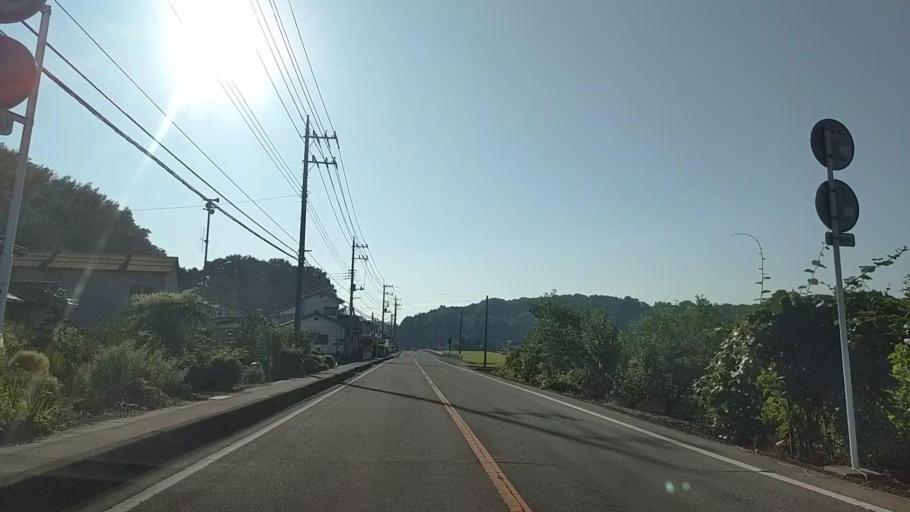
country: JP
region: Gunma
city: Annaka
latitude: 36.3483
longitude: 138.8725
